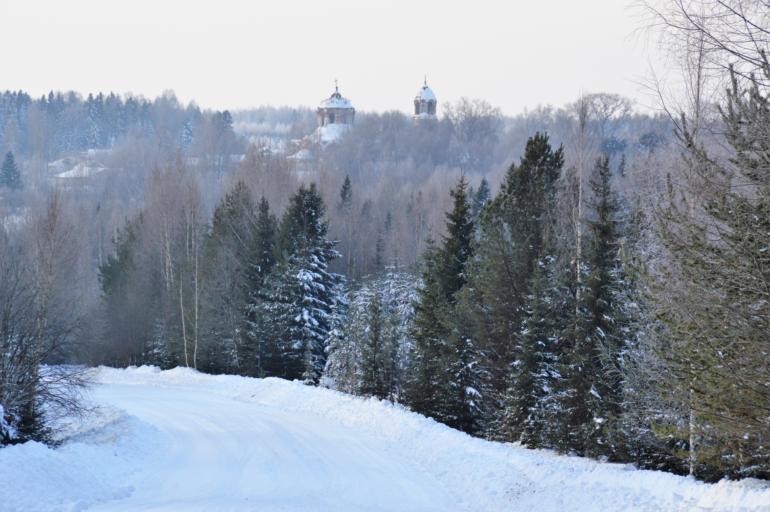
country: RU
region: Kirov
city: Nizhneivkino
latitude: 57.9732
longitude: 49.6697
